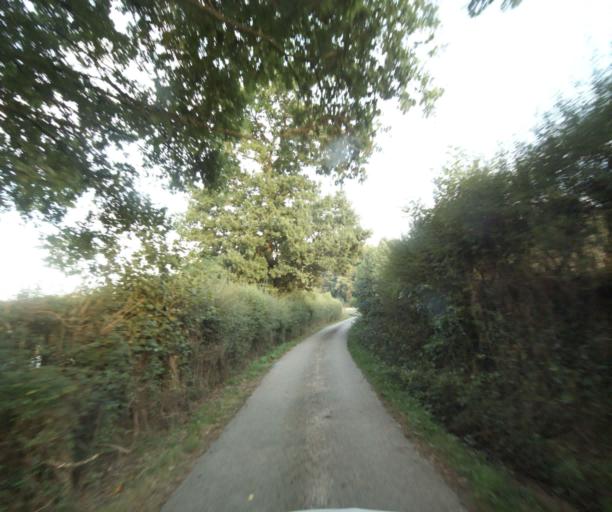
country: FR
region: Bourgogne
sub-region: Departement de Saone-et-Loire
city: Matour
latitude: 46.3935
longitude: 4.4076
